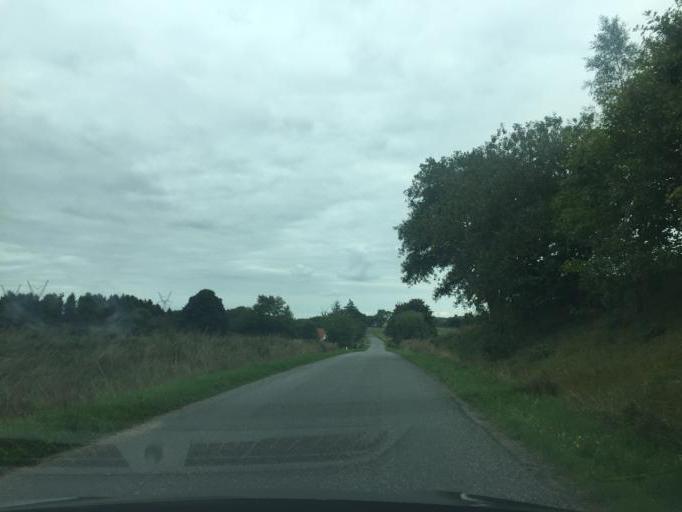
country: DK
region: South Denmark
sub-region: Assens Kommune
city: Tommerup Stationsby
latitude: 55.3781
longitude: 10.2228
